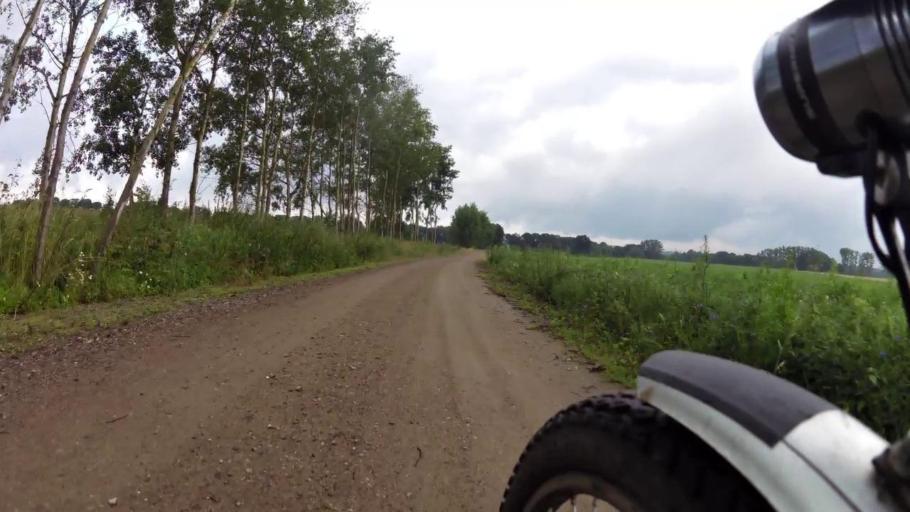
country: PL
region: West Pomeranian Voivodeship
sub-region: Powiat lobeski
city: Lobez
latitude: 53.7228
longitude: 15.6318
